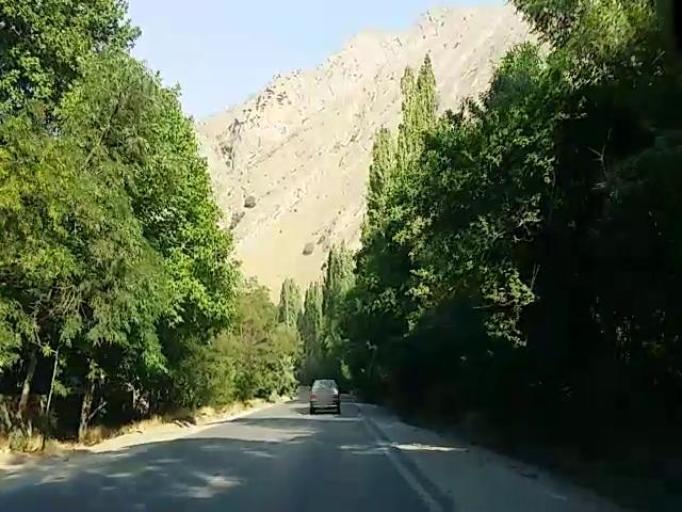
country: IR
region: Tehran
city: Tajrish
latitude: 36.0297
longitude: 51.2241
